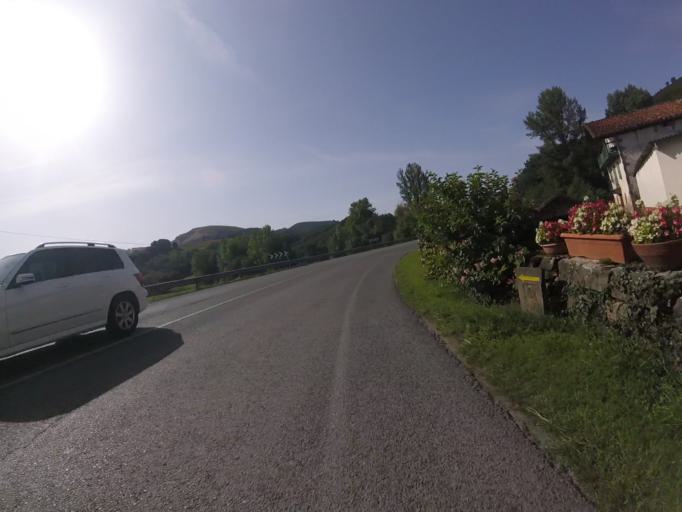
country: ES
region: Navarre
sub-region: Provincia de Navarra
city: Zugarramurdi
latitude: 43.1619
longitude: -1.4958
